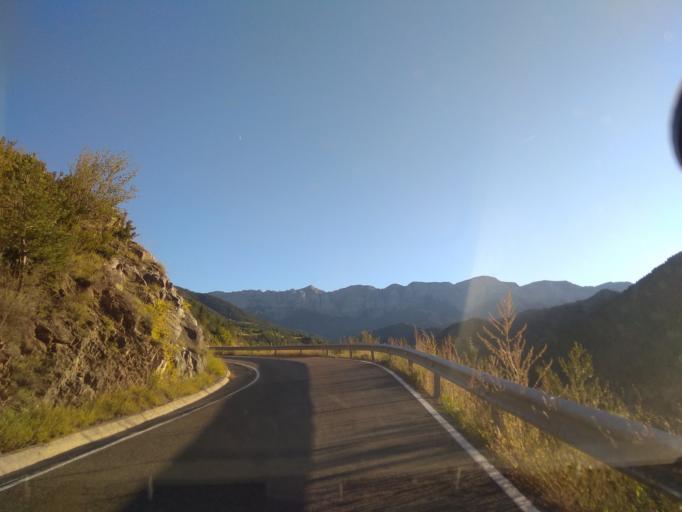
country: ES
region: Catalonia
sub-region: Provincia de Lleida
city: Lles de Cerdanya
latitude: 42.3537
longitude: 1.6895
